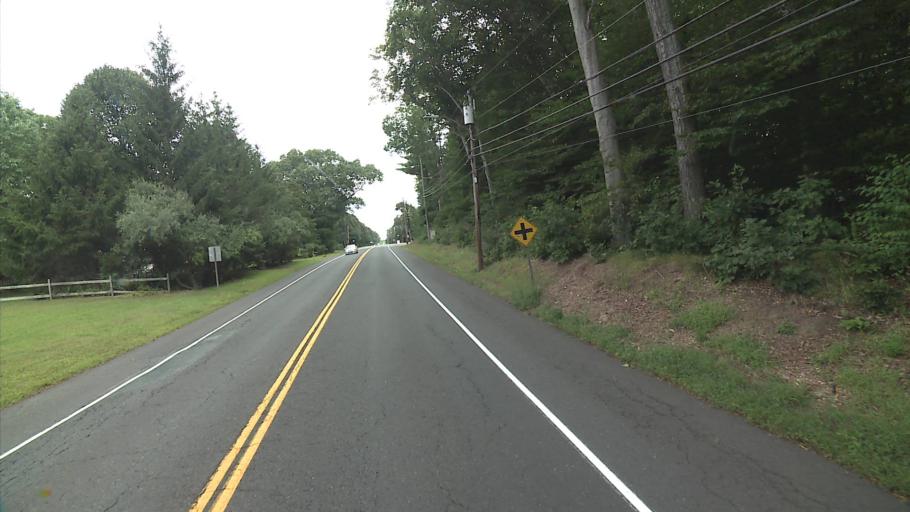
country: US
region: Connecticut
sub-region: Hartford County
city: Tariffville
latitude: 41.8718
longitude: -72.7444
